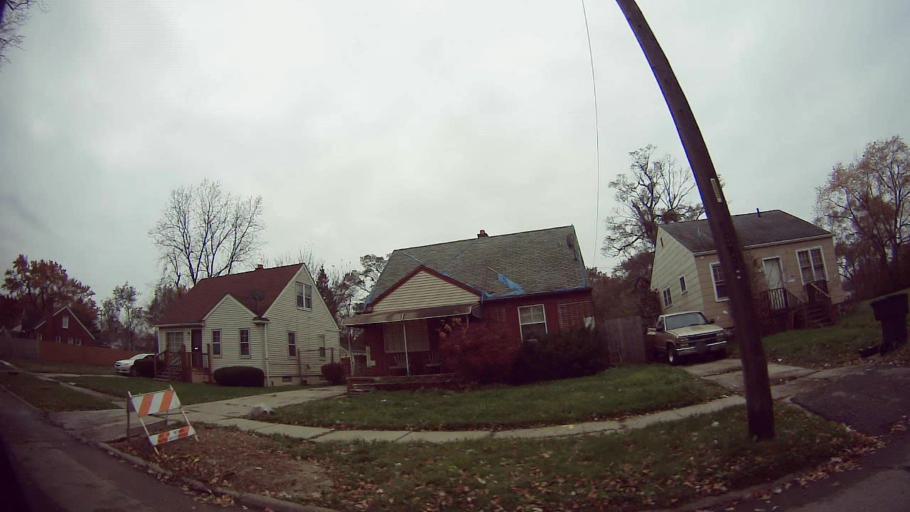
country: US
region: Michigan
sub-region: Wayne County
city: Dearborn Heights
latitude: 42.3565
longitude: -83.2371
